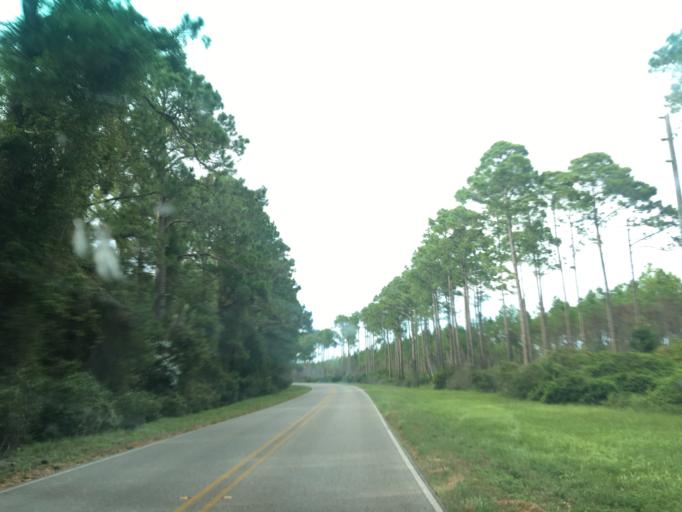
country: US
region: Florida
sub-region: Wakulla County
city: Crawfordville
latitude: 29.9318
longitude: -84.3787
